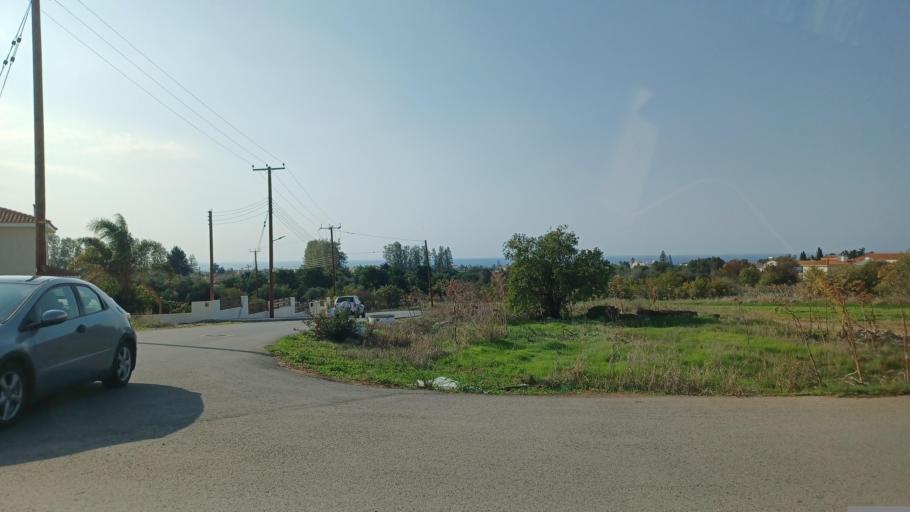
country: CY
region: Pafos
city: Empa
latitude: 34.8032
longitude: 32.4195
